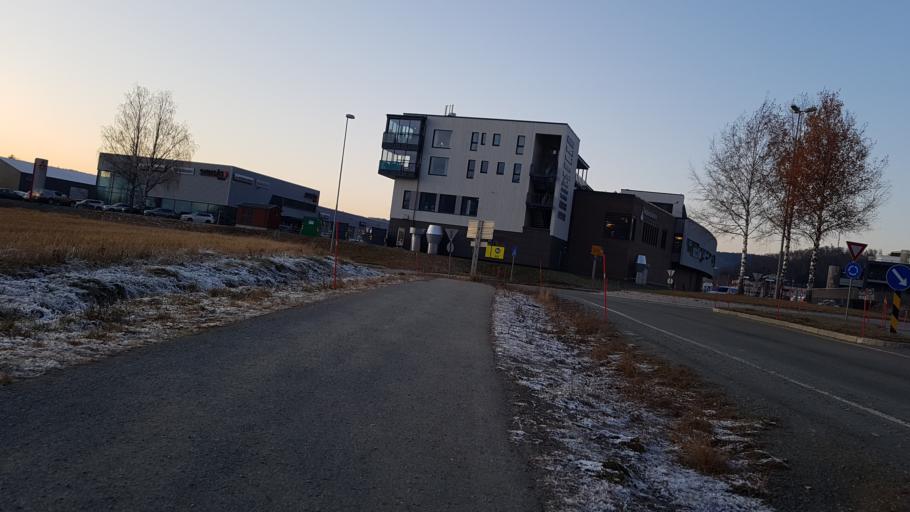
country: NO
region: Sor-Trondelag
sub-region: Melhus
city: Melhus
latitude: 63.2829
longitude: 10.2824
